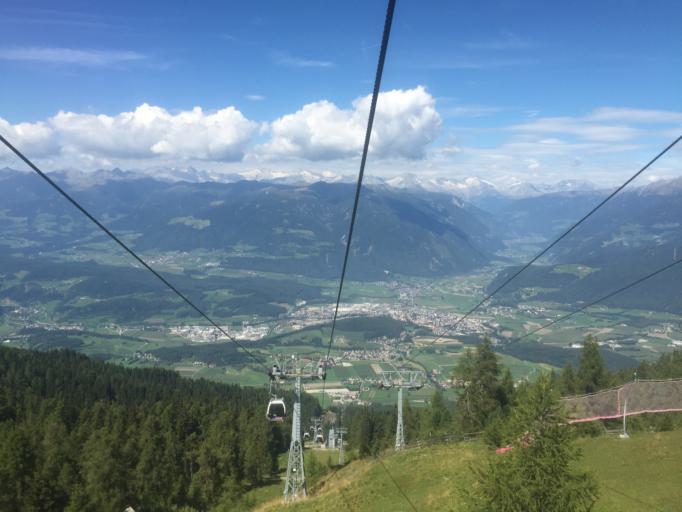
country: IT
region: Trentino-Alto Adige
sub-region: Bolzano
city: Riscone
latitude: 46.7443
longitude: 11.9548
